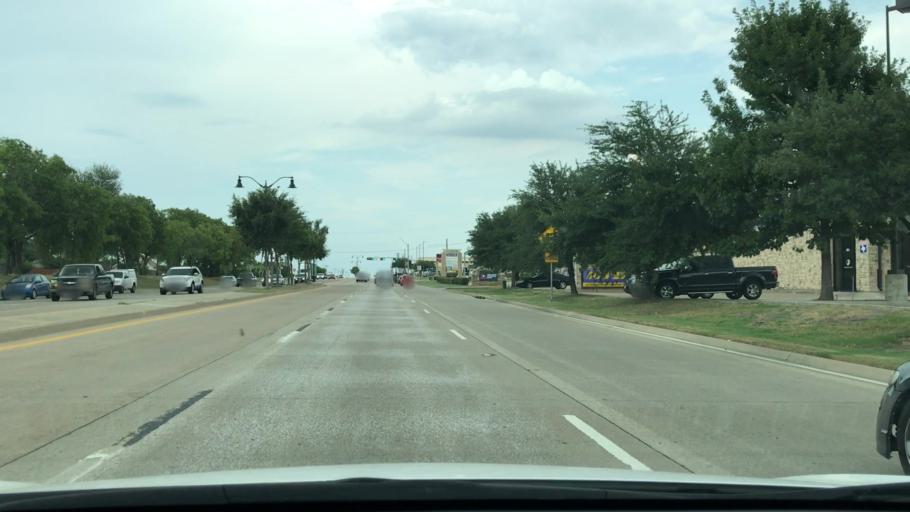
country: US
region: Texas
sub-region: Dallas County
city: Sachse
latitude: 32.9714
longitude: -96.6029
